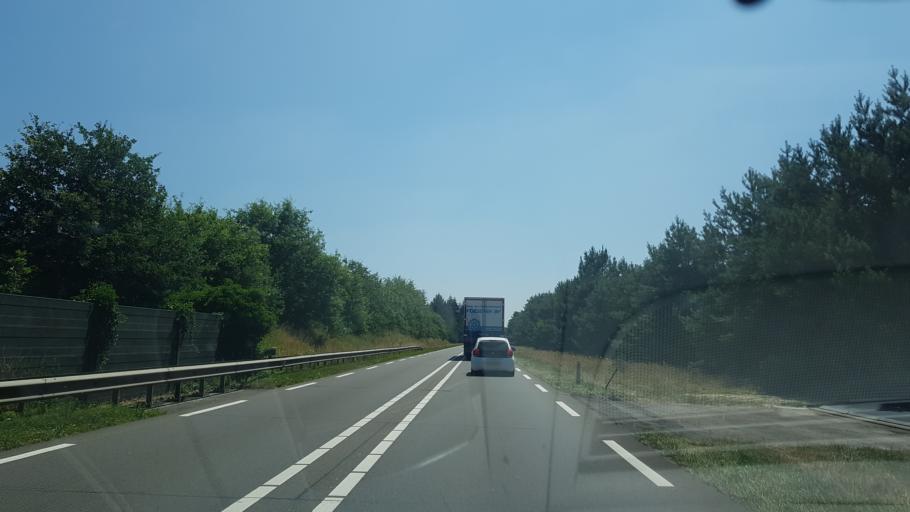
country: NL
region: North Brabant
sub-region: Gemeente Helmond
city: Helmond
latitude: 51.4827
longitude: 5.7122
